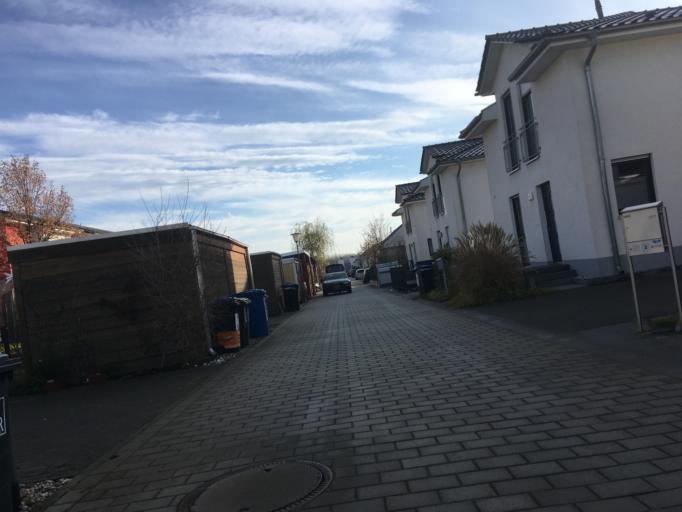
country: DE
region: Berlin
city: Karlshorst
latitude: 52.4761
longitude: 13.5335
